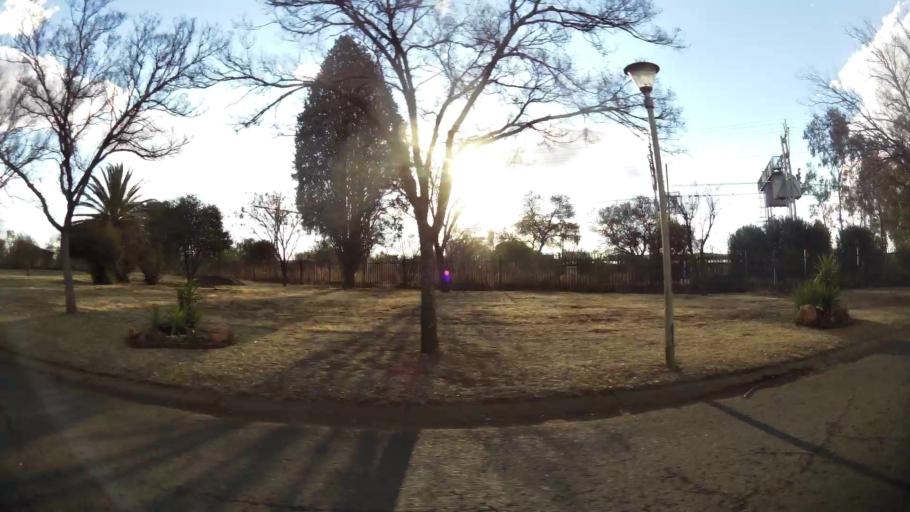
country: ZA
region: North-West
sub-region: Dr Kenneth Kaunda District Municipality
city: Potchefstroom
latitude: -26.7209
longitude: 27.0827
